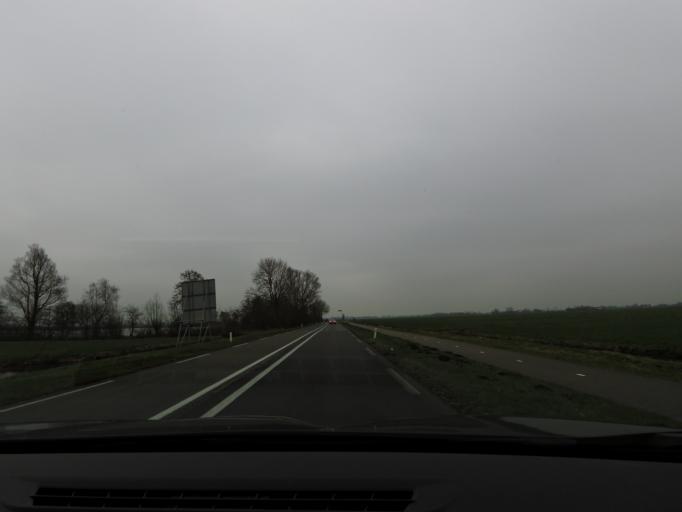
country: NL
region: Utrecht
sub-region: Gemeente De Ronde Venen
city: Mijdrecht
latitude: 52.1578
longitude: 4.9110
